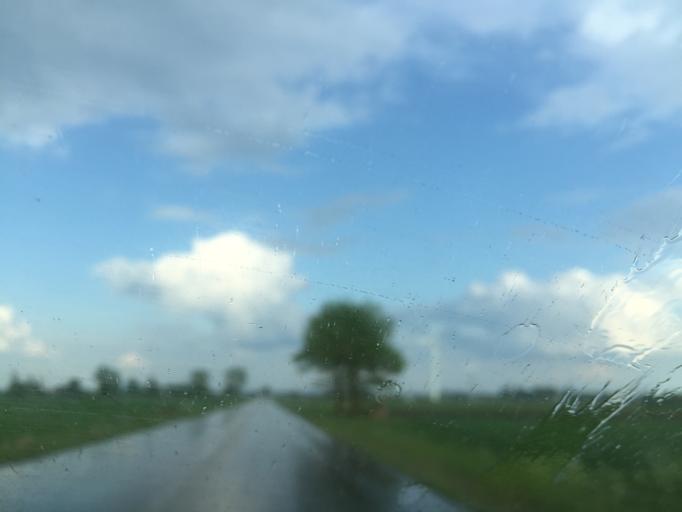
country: LT
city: Salantai
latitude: 56.0617
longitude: 21.4841
